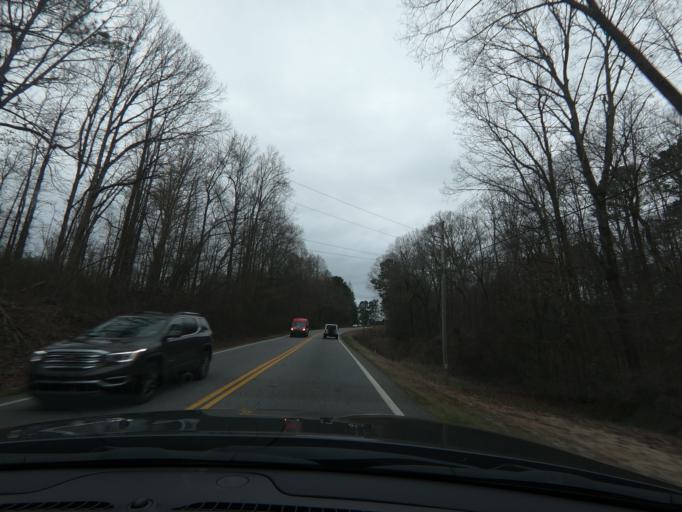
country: US
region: Georgia
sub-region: Dawson County
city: Dawsonville
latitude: 34.3430
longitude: -84.1177
